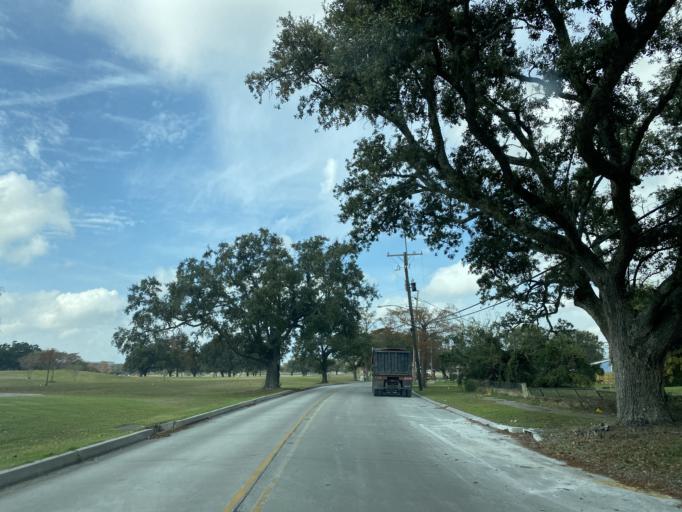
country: US
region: Louisiana
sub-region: Saint Bernard Parish
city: Arabi
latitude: 30.0228
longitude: -90.0379
